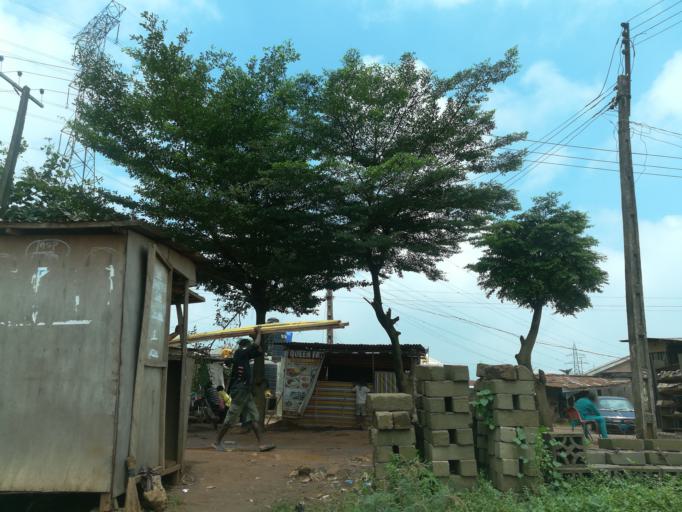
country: NG
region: Lagos
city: Ikorodu
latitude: 6.6806
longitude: 3.5113
